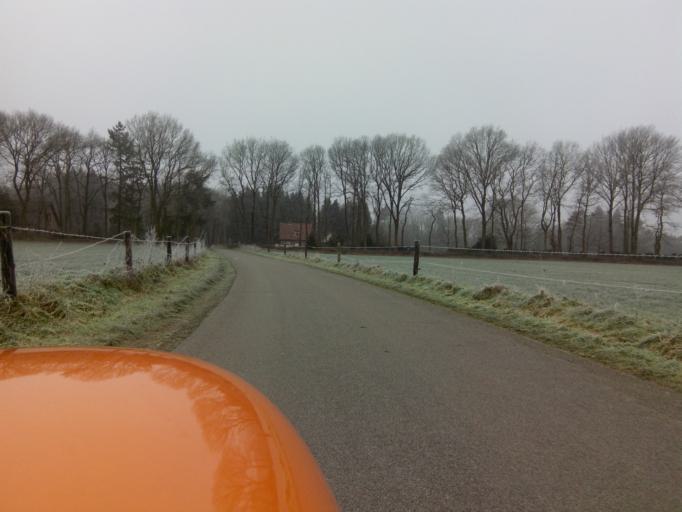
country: NL
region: Gelderland
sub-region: Gemeente Barneveld
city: Garderen
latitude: 52.2298
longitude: 5.7040
